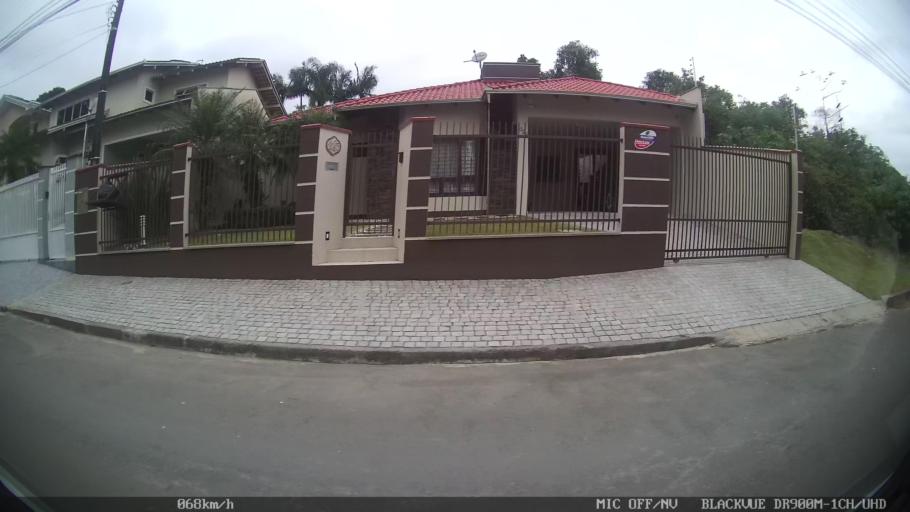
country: BR
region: Santa Catarina
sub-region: Joinville
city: Joinville
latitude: -26.2729
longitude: -48.8666
